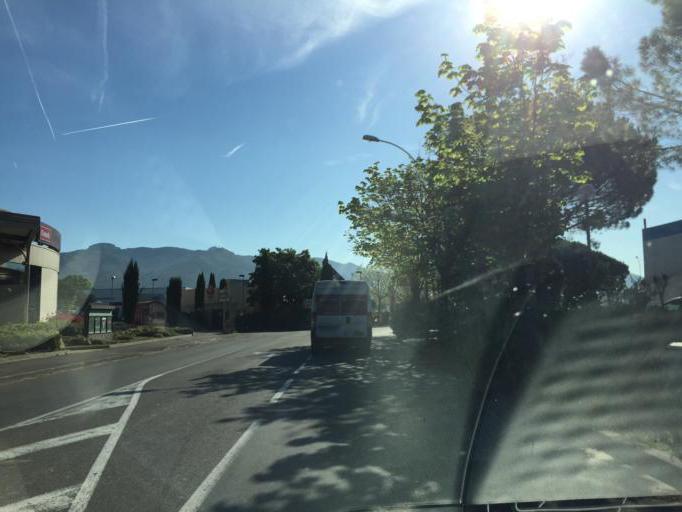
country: FR
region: Provence-Alpes-Cote d'Azur
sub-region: Departement des Bouches-du-Rhone
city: Aubagne
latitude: 43.2917
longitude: 5.5920
